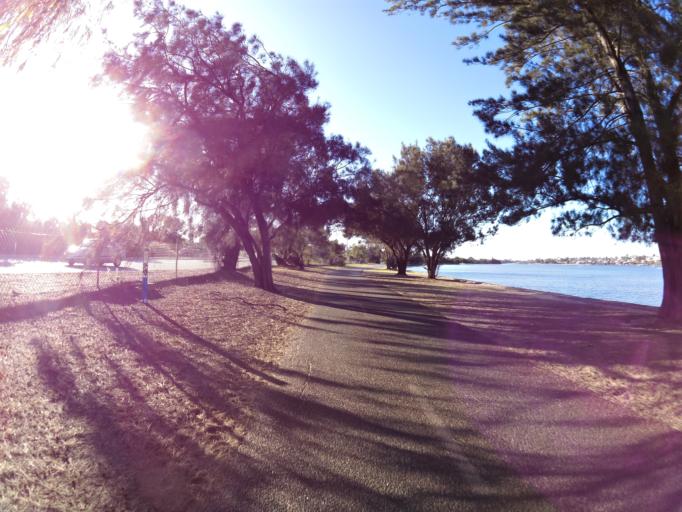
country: AU
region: Western Australia
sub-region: South Perth
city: Manning
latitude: -32.0118
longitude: 115.8562
